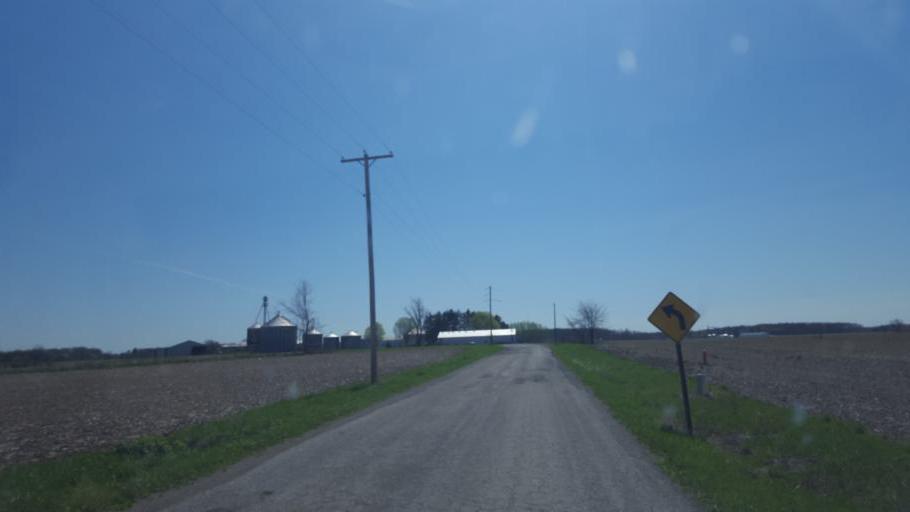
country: US
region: Ohio
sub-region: Morrow County
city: Mount Gilead
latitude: 40.6135
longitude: -82.8719
